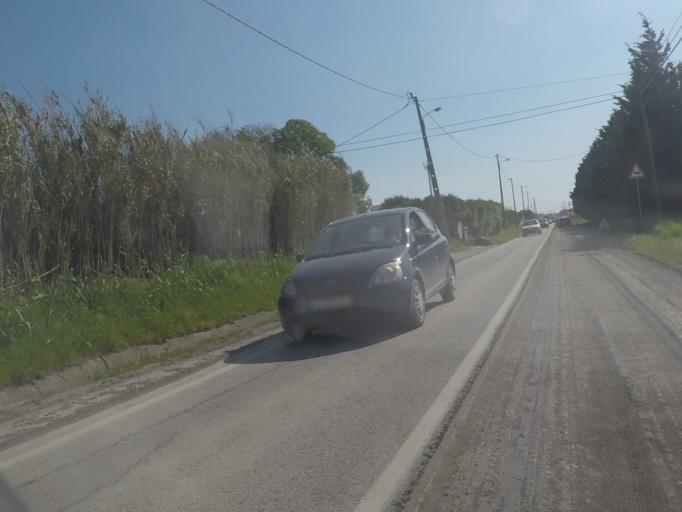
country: PT
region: Setubal
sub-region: Sesimbra
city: Sesimbra
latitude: 38.4349
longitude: -9.1811
